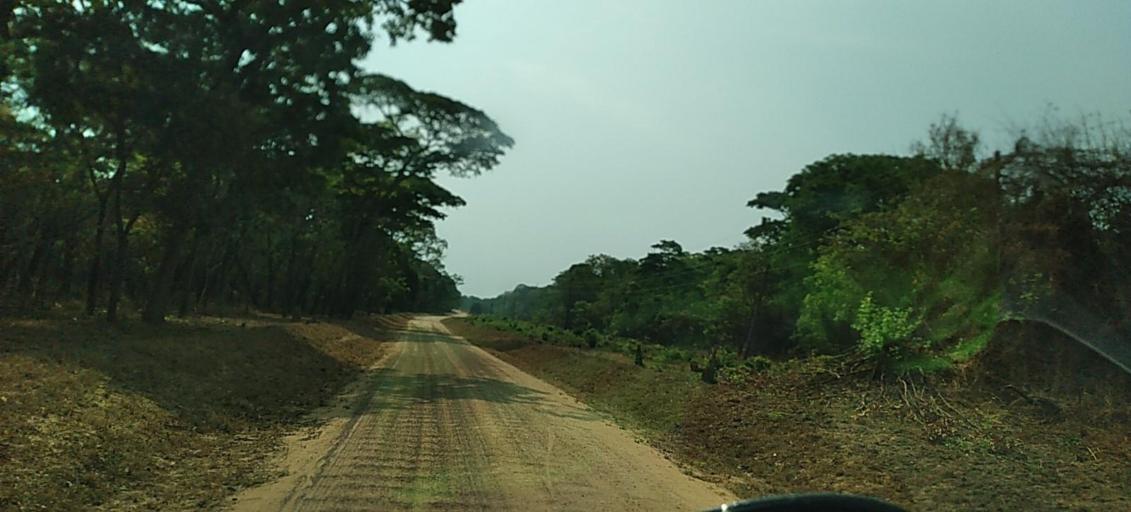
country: ZM
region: North-Western
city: Solwezi
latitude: -12.6851
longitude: 26.3928
